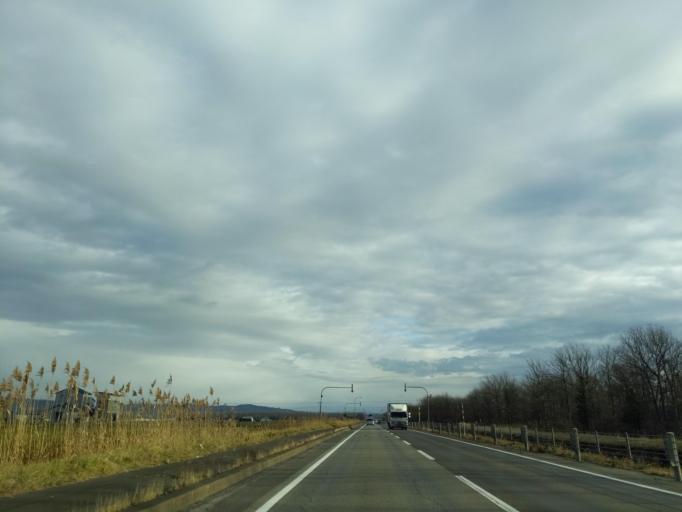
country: JP
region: Hokkaido
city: Kitahiroshima
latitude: 42.9749
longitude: 141.6497
